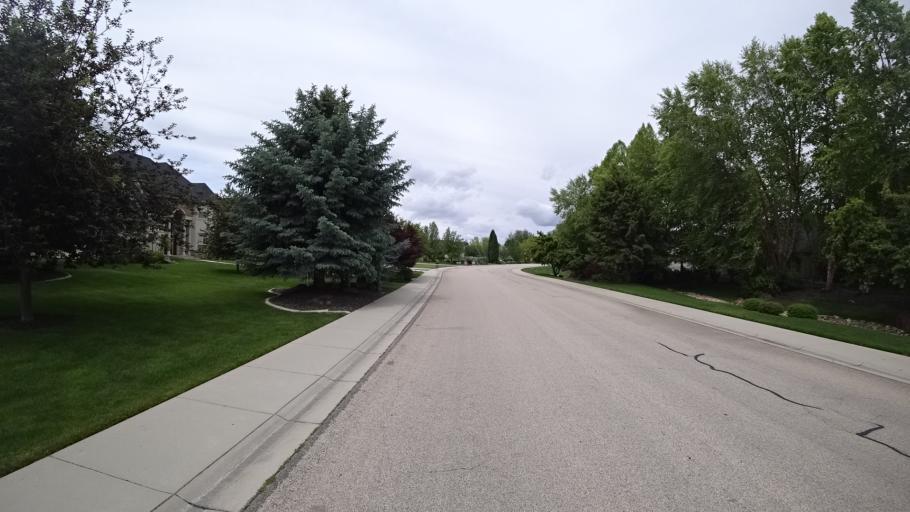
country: US
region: Idaho
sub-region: Ada County
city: Eagle
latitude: 43.6762
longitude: -116.3115
